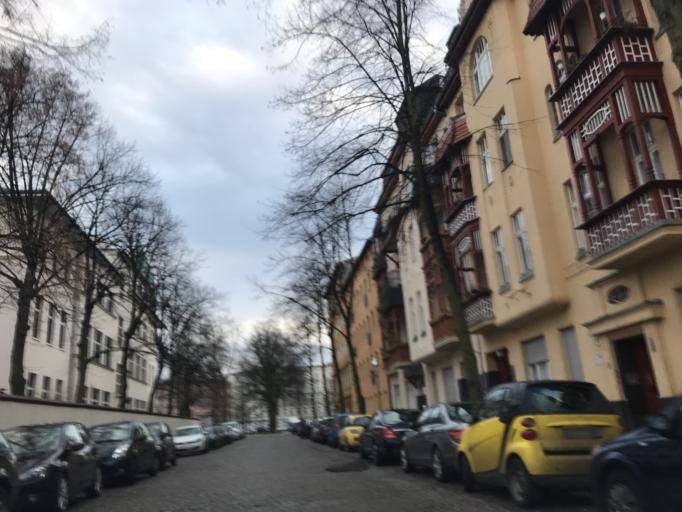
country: DE
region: Berlin
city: Spandau
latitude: 52.5496
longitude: 13.2038
